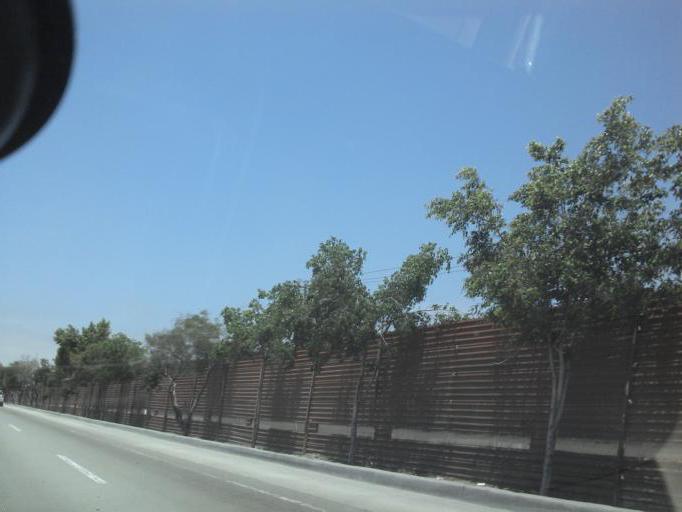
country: MX
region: Baja California
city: Tijuana
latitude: 32.5413
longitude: -117.0429
